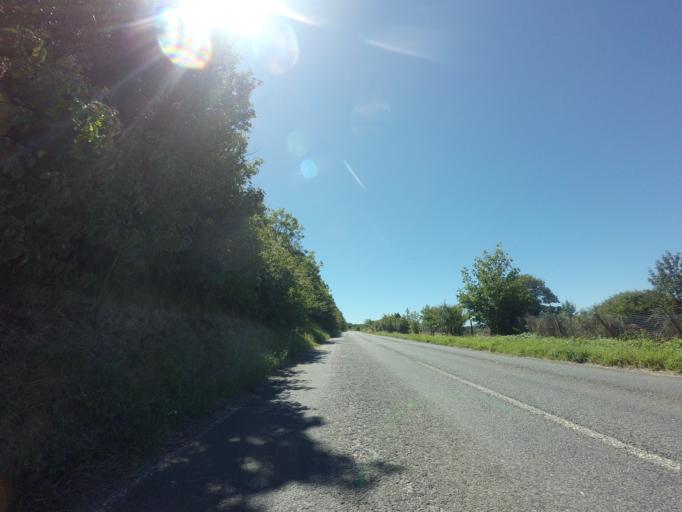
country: GB
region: England
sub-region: Kent
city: Eastry
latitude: 51.2098
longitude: 1.2998
